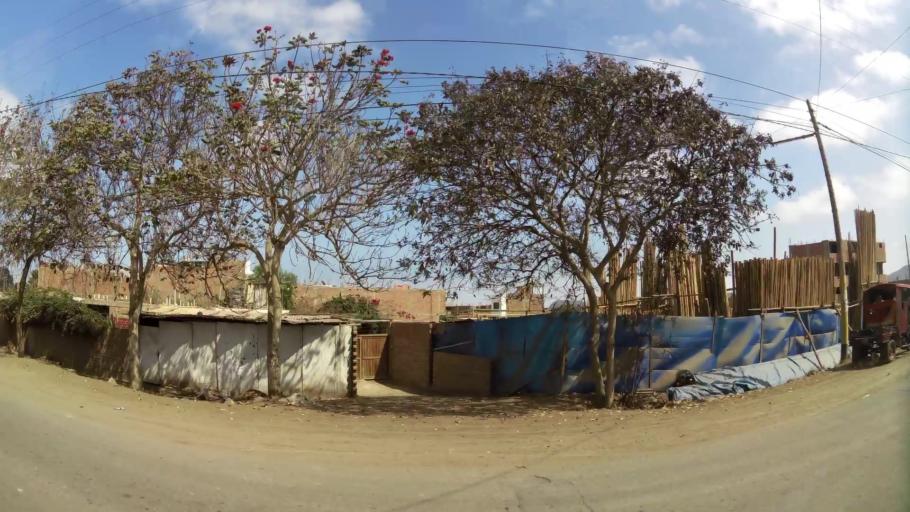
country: PE
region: Lima
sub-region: Provincia de Canete
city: Mala
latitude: -12.6674
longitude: -76.6313
